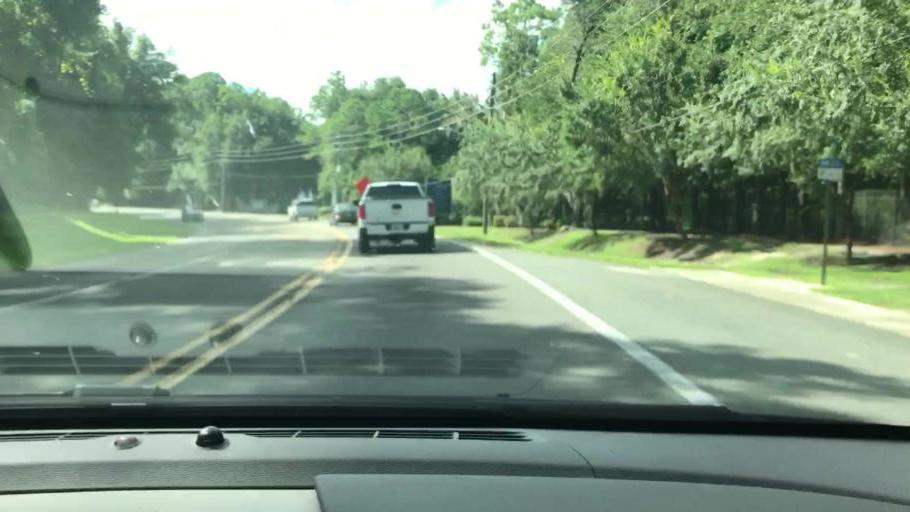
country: US
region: Florida
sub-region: Alachua County
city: Gainesville
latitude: 29.6518
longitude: -82.4089
